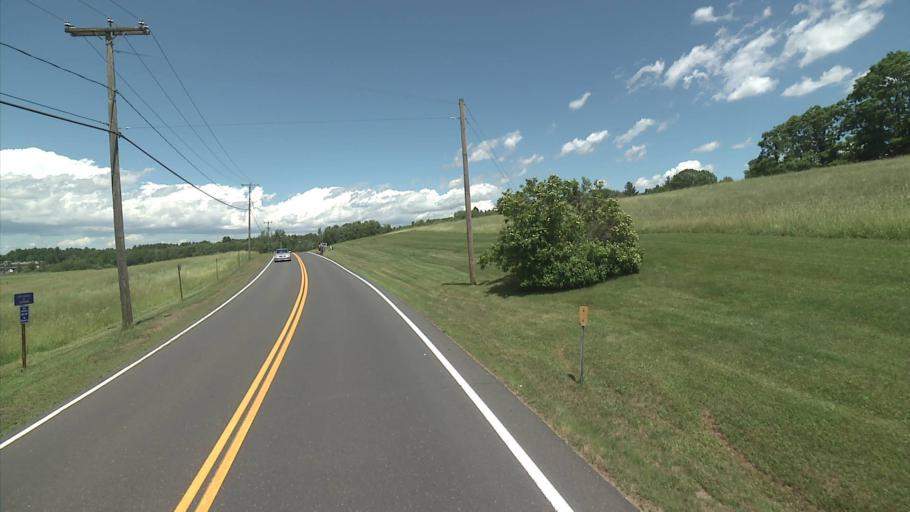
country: US
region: Massachusetts
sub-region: Hampden County
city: East Longmeadow
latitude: 42.0181
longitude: -72.5026
